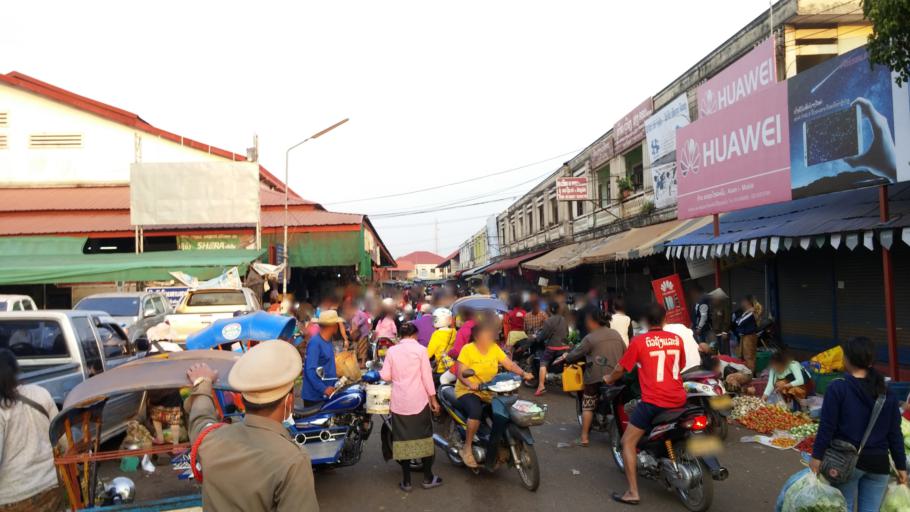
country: LA
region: Champasak
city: Pakxe
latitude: 15.1168
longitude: 105.8152
